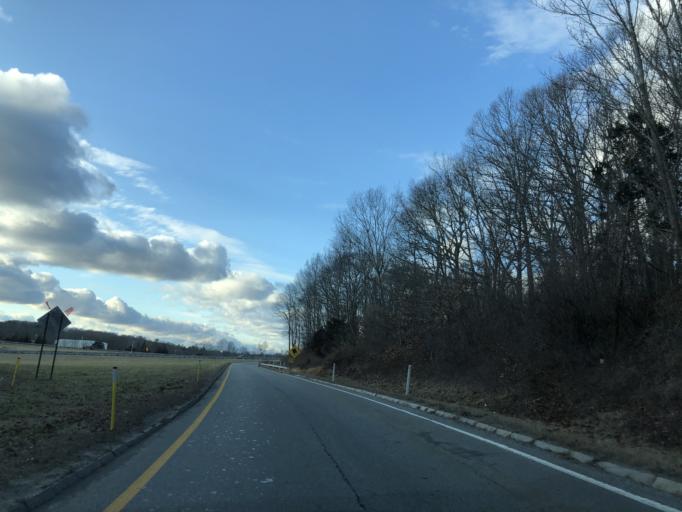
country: US
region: Massachusetts
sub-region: Bristol County
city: New Bedford
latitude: 41.6535
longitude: -70.9512
